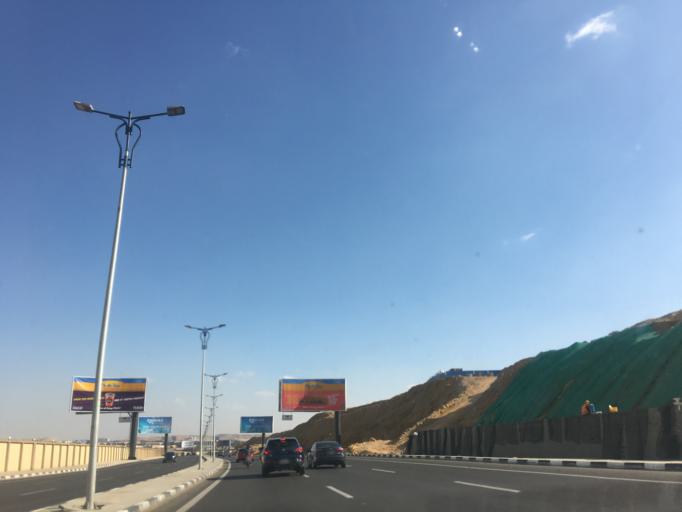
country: EG
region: Muhafazat al Qahirah
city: Cairo
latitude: 30.0280
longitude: 31.3133
